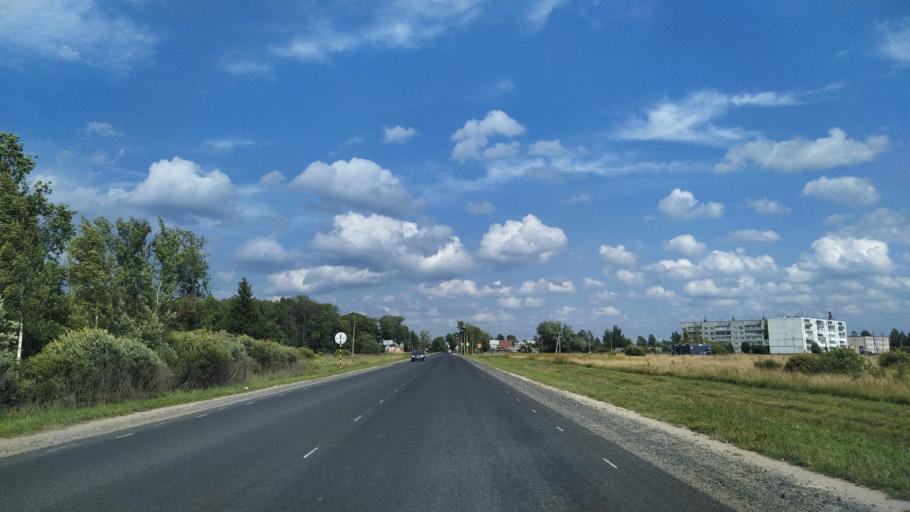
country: RU
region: Pskov
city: Porkhov
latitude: 57.7590
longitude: 29.5389
